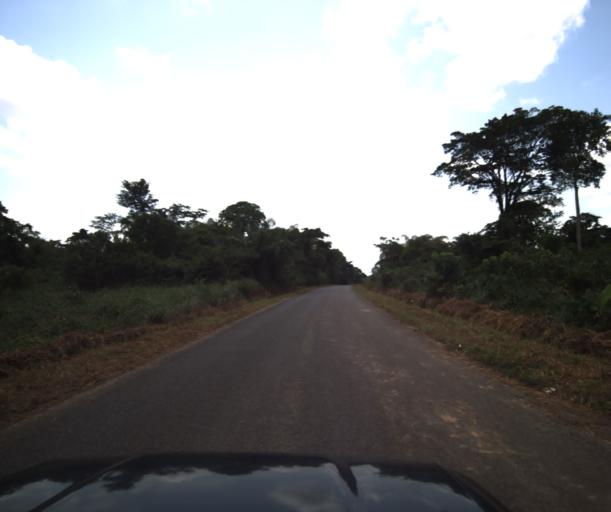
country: CM
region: Centre
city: Eseka
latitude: 3.7061
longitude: 10.7917
